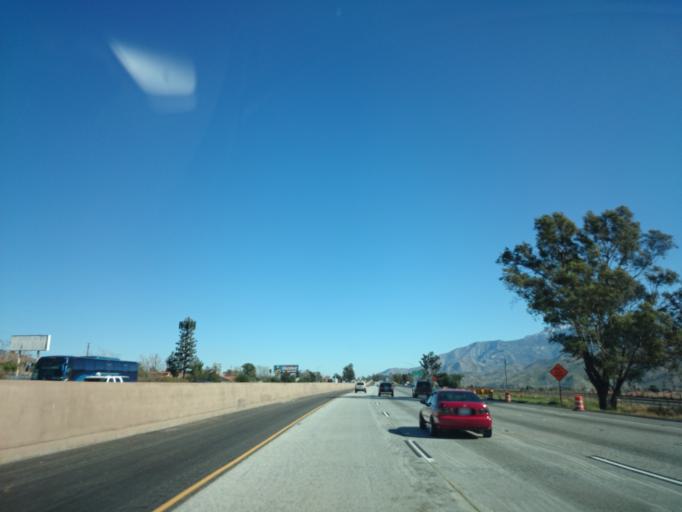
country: US
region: California
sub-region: Riverside County
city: Banning
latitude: 33.9257
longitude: -116.9194
